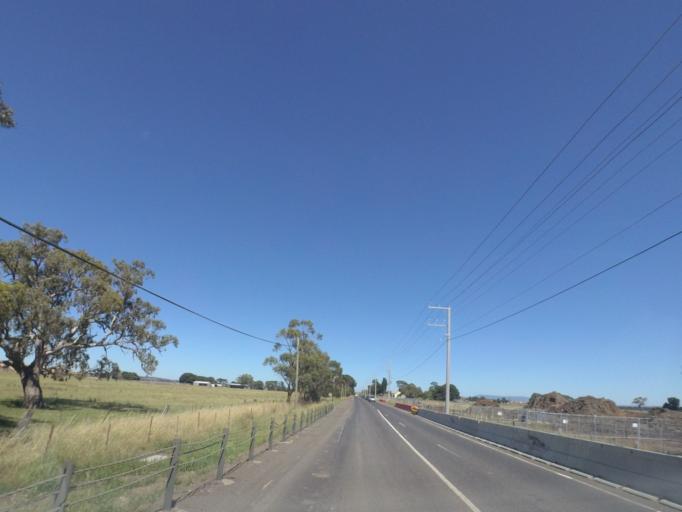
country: AU
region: Victoria
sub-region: Hume
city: Craigieburn
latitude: -37.5449
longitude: 144.9912
